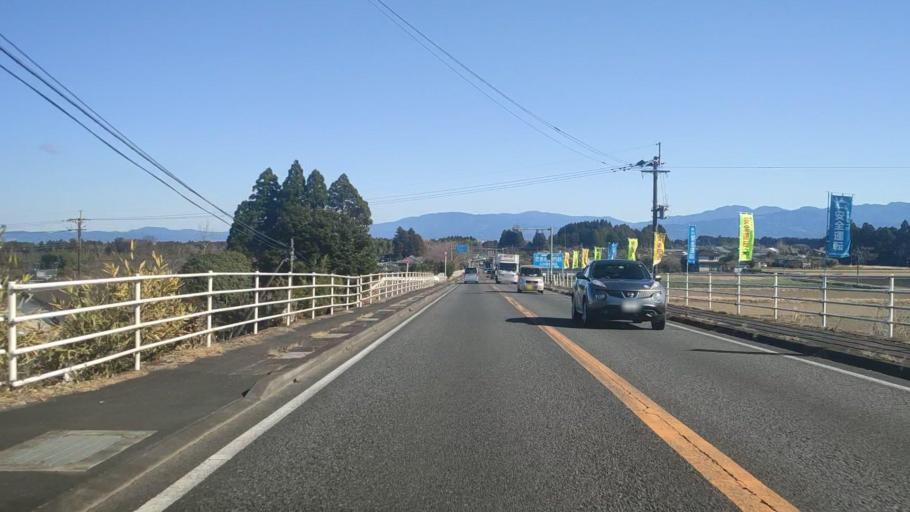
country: JP
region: Kagoshima
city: Sueyoshicho-ninokata
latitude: 31.7015
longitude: 131.0170
